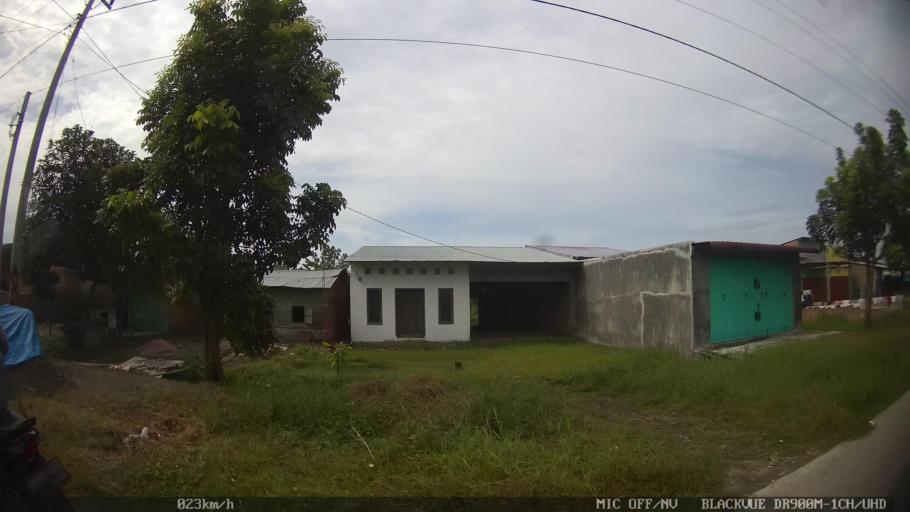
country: ID
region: North Sumatra
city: Percut
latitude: 3.6199
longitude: 98.7637
